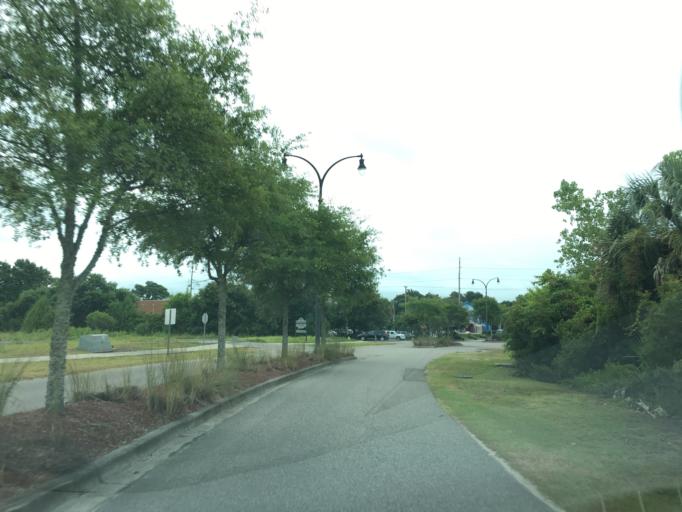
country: US
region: South Carolina
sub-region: Horry County
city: North Myrtle Beach
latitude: 33.8023
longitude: -78.7333
